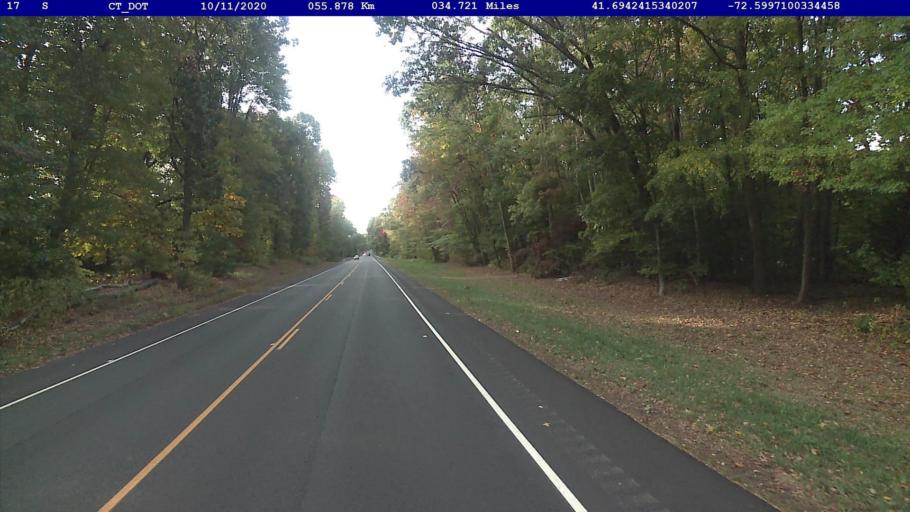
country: US
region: Connecticut
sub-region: Hartford County
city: Glastonbury Center
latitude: 41.6943
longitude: -72.5998
